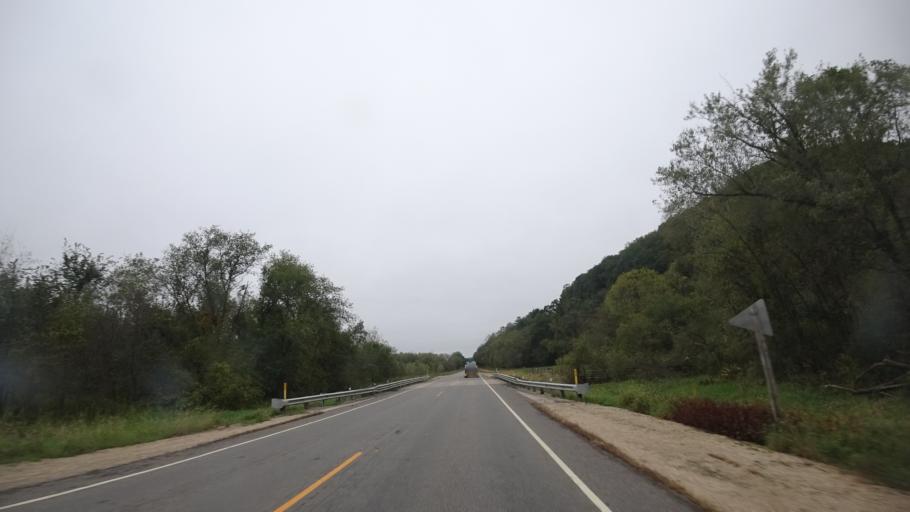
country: US
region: Wisconsin
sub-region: Crawford County
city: Prairie du Chien
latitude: 43.0595
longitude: -90.9584
